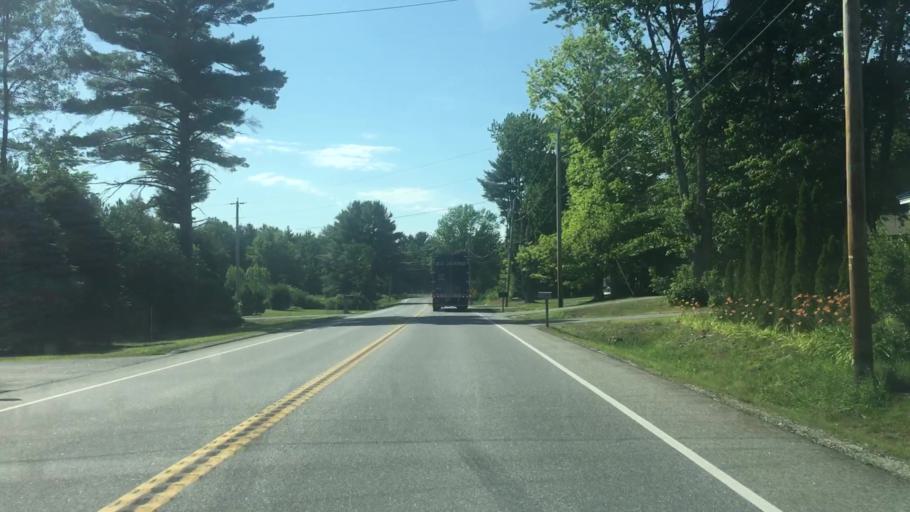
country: US
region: Maine
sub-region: York County
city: Buxton
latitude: 43.5698
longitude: -70.5093
